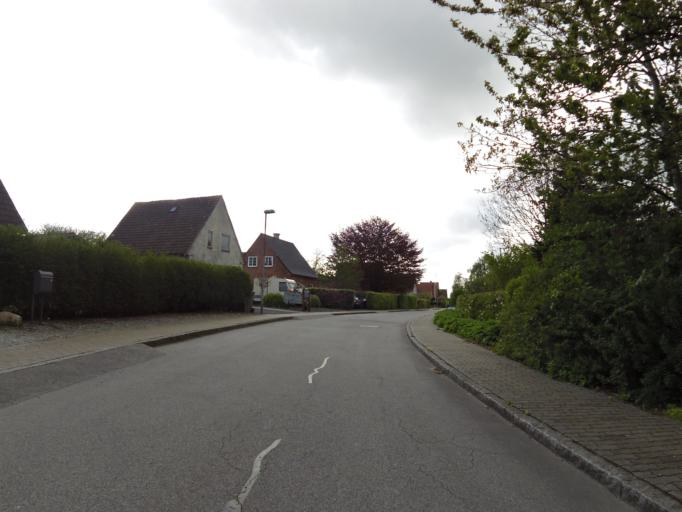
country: DK
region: South Denmark
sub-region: Haderslev Kommune
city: Gram
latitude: 55.2949
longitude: 9.0509
